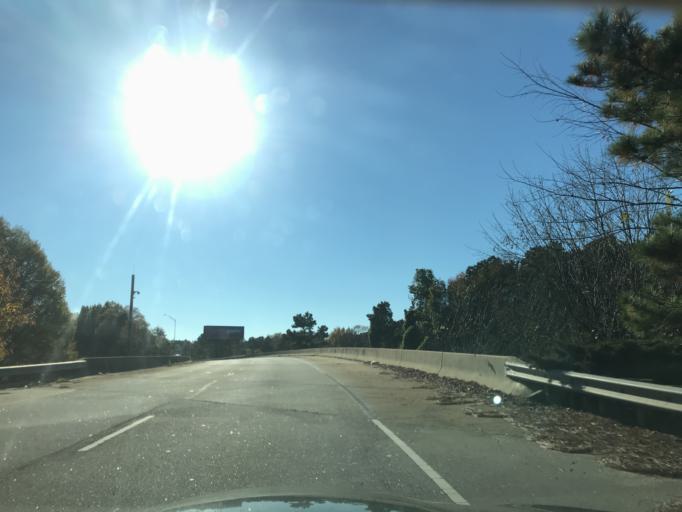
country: US
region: North Carolina
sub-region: Wake County
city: Raleigh
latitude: 35.7424
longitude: -78.6484
